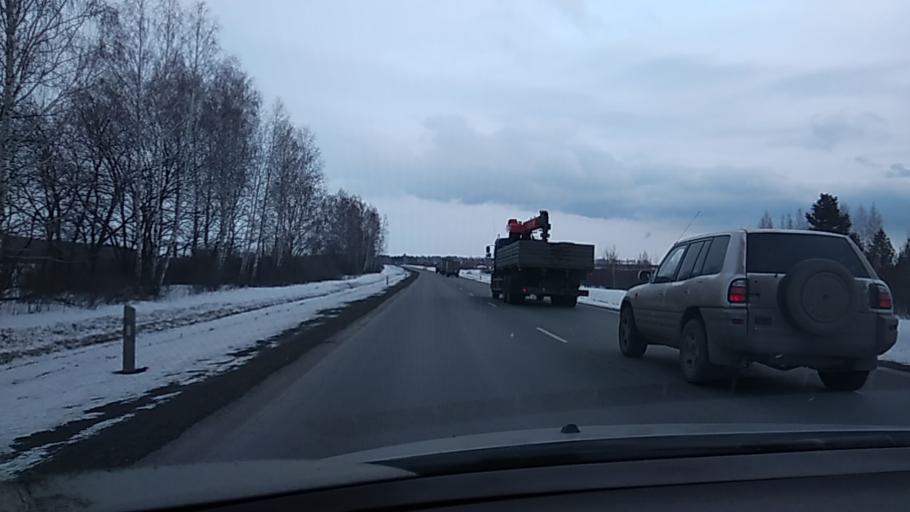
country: RU
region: Sverdlovsk
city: Sovkhoznyy
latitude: 56.5104
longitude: 61.4591
